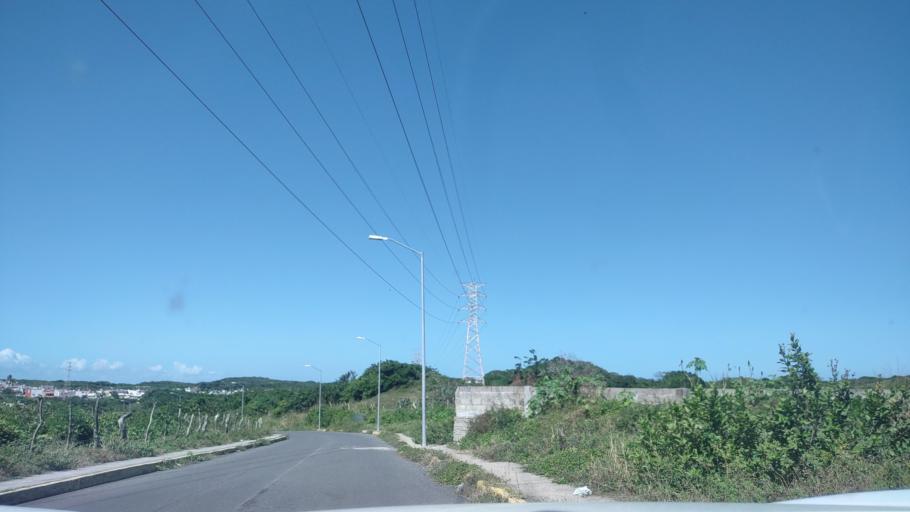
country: MX
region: Veracruz
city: Heroica Alvarado
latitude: 18.7803
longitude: -95.7664
